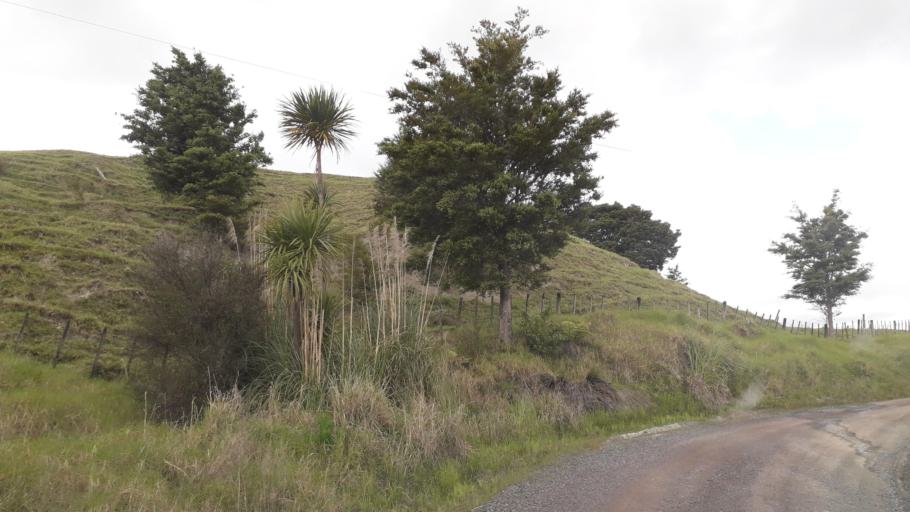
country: NZ
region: Northland
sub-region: Far North District
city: Waimate North
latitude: -35.3115
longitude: 173.5646
